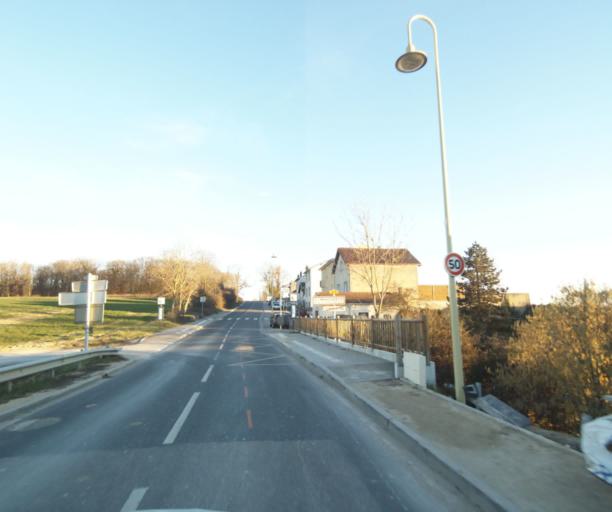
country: FR
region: Lorraine
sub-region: Departement de Meurthe-et-Moselle
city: Laneuveville-devant-Nancy
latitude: 48.6723
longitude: 6.2266
